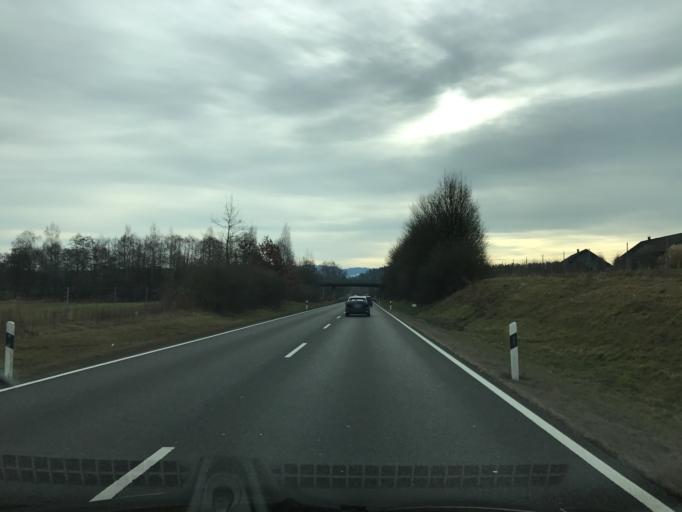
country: DE
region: Bavaria
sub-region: Swabia
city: Bodolz
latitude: 47.5863
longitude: 9.6555
